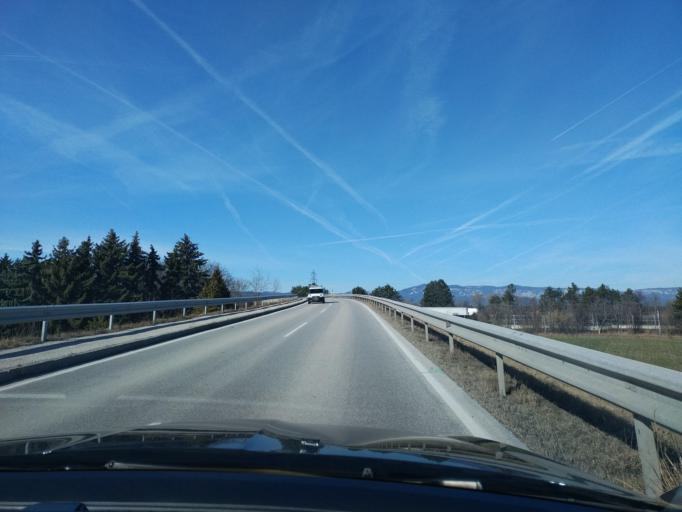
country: AT
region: Lower Austria
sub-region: Politischer Bezirk Neunkirchen
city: Breitenau
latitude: 47.7327
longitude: 16.1622
